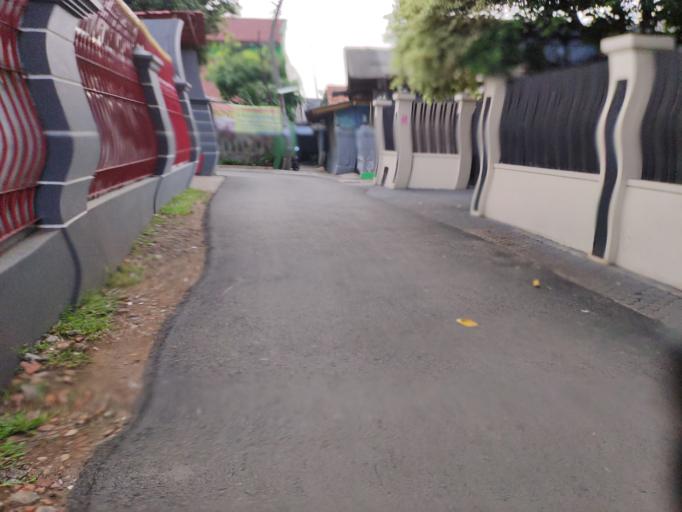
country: ID
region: West Java
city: Pamulang
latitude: -6.3237
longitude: 106.7995
